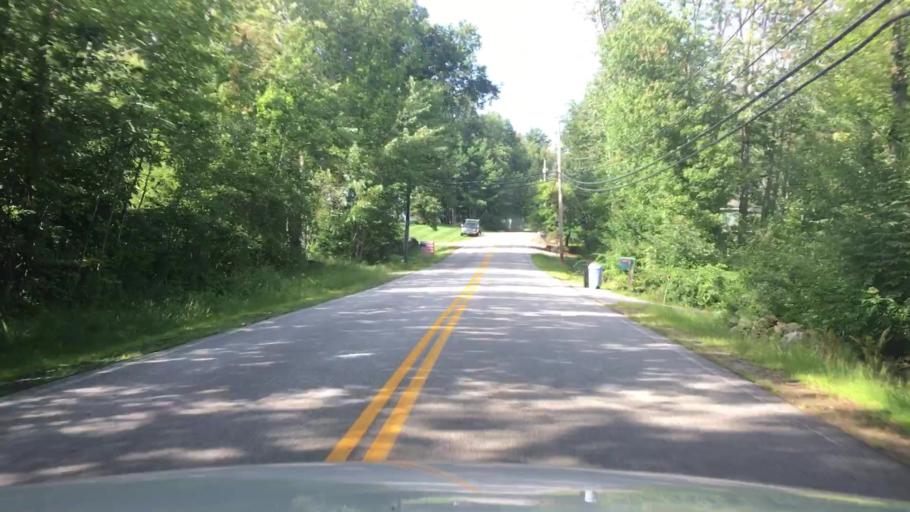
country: US
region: New Hampshire
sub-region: Belknap County
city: Gilford
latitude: 43.5434
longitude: -71.4160
